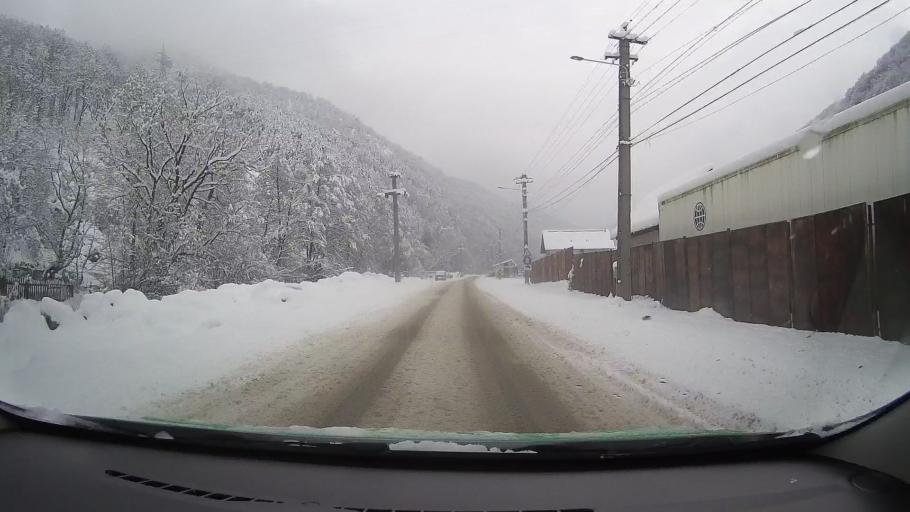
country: RO
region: Alba
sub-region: Comuna Sugag
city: Dobra
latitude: 45.7676
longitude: 23.6438
